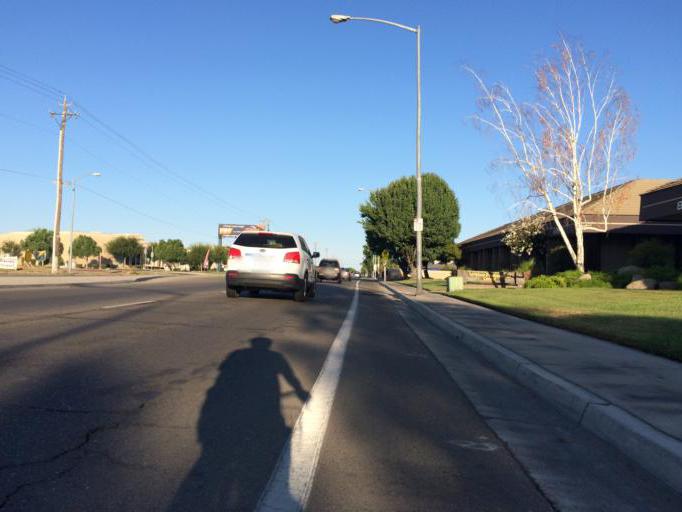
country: US
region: California
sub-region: Fresno County
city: Tarpey Village
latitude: 36.7943
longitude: -119.7283
